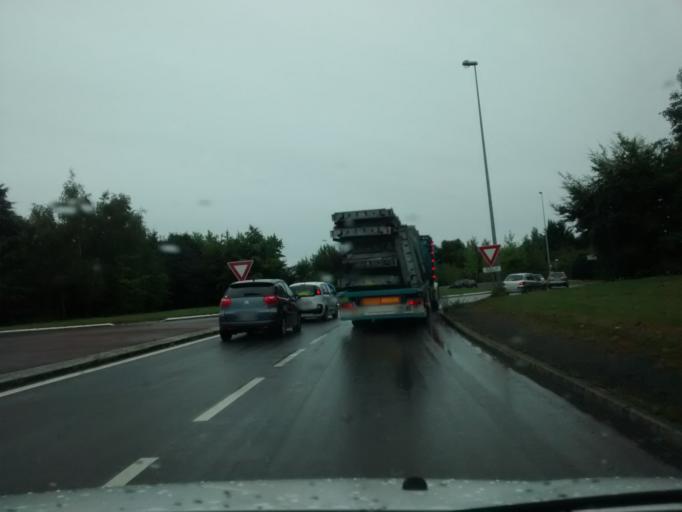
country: FR
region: Brittany
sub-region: Departement d'Ille-et-Vilaine
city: Vern-sur-Seiche
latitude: 48.0502
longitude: -1.6088
